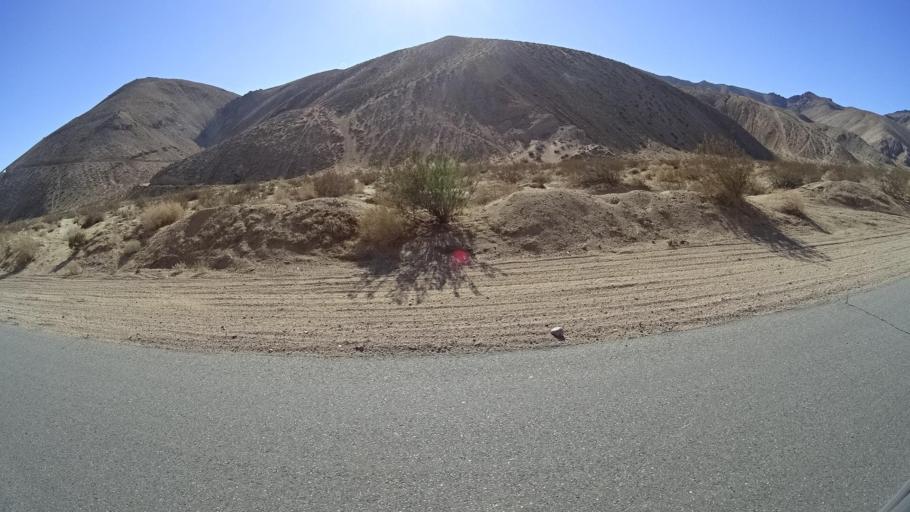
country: US
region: California
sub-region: Kern County
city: California City
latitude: 35.3163
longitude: -118.0522
